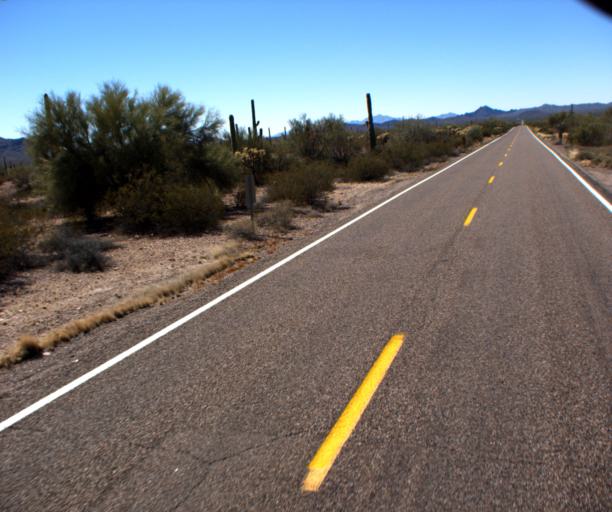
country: MX
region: Sonora
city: Sonoyta
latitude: 32.0693
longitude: -112.7837
